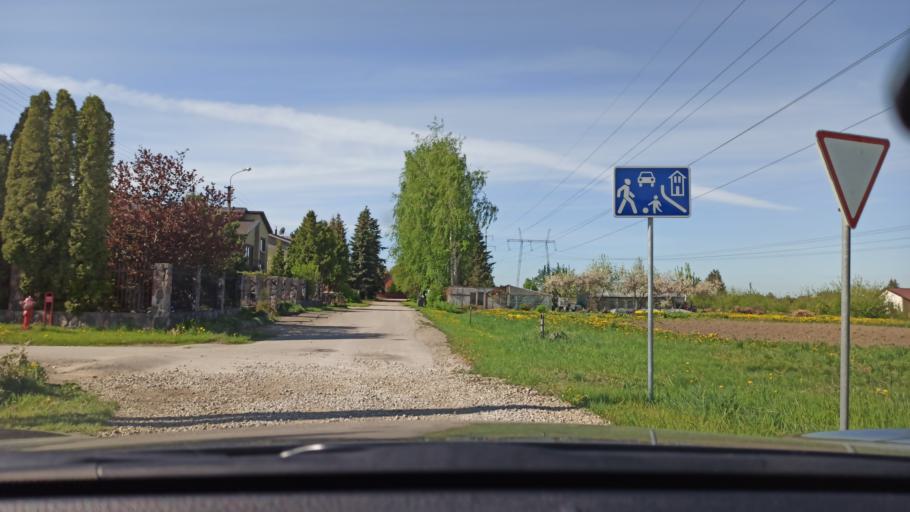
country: LT
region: Siauliu apskritis
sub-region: Siauliai
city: Siauliai
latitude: 55.9640
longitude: 23.2950
